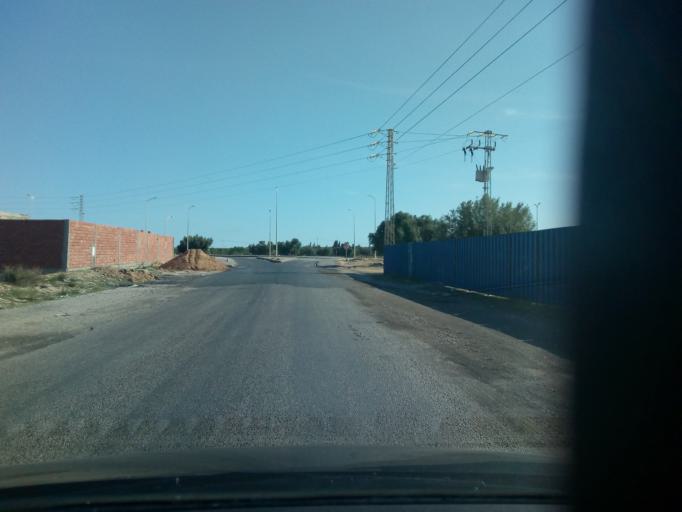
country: TN
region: Safaqis
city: Sfax
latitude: 34.7288
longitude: 10.6157
